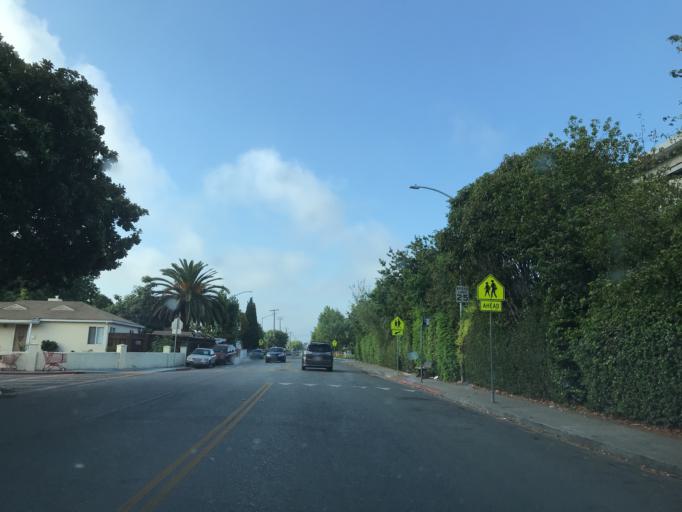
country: US
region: California
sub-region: San Mateo County
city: East Palo Alto
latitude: 37.4642
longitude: -122.1302
